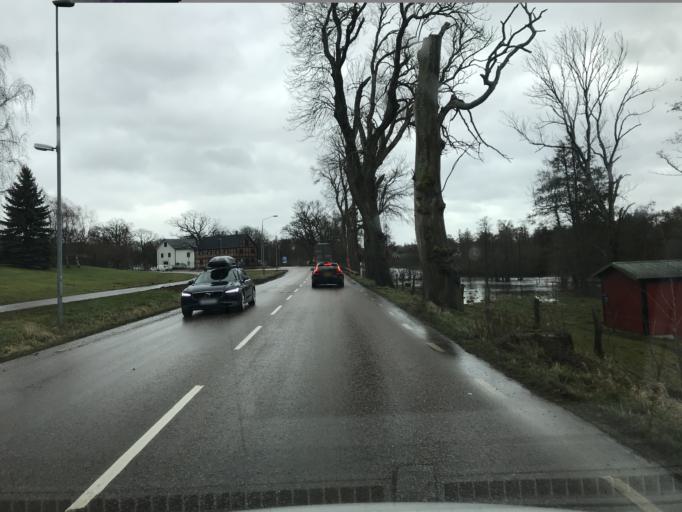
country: SE
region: Skane
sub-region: Klippans Kommun
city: Ljungbyhed
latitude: 56.0834
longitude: 13.2372
